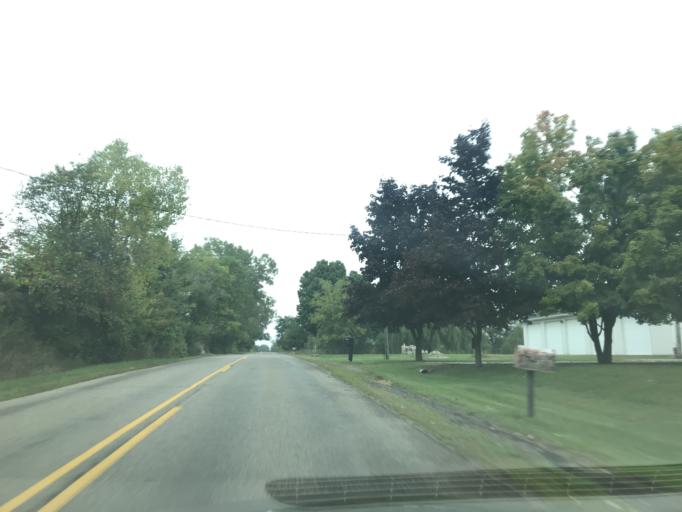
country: US
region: Michigan
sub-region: Eaton County
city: Eaton Rapids
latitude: 42.5747
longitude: -84.6611
